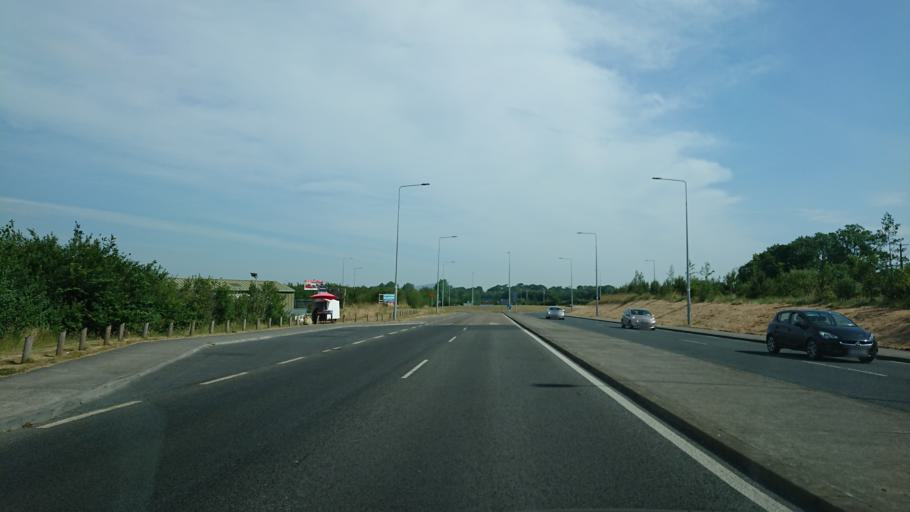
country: IE
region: Munster
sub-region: Waterford
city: Waterford
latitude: 52.2756
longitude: -7.1324
